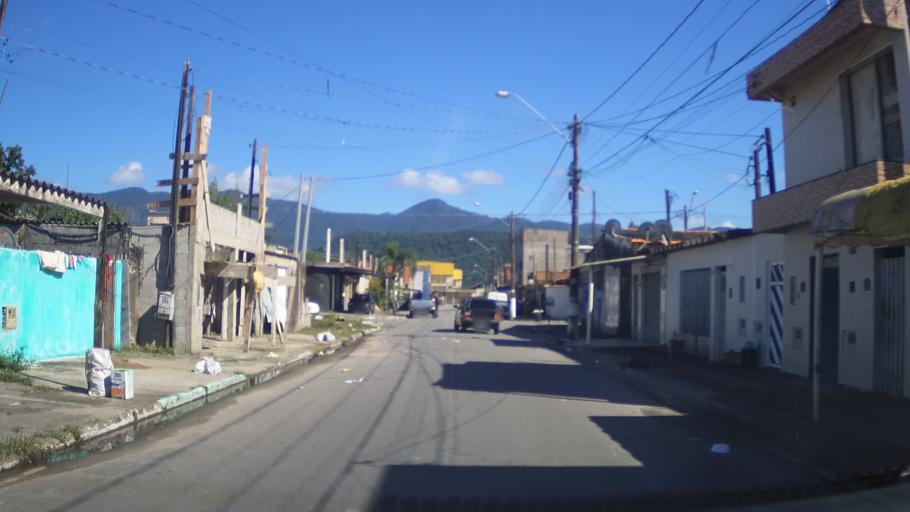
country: BR
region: Sao Paulo
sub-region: Praia Grande
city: Praia Grande
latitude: -24.0269
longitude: -46.5170
